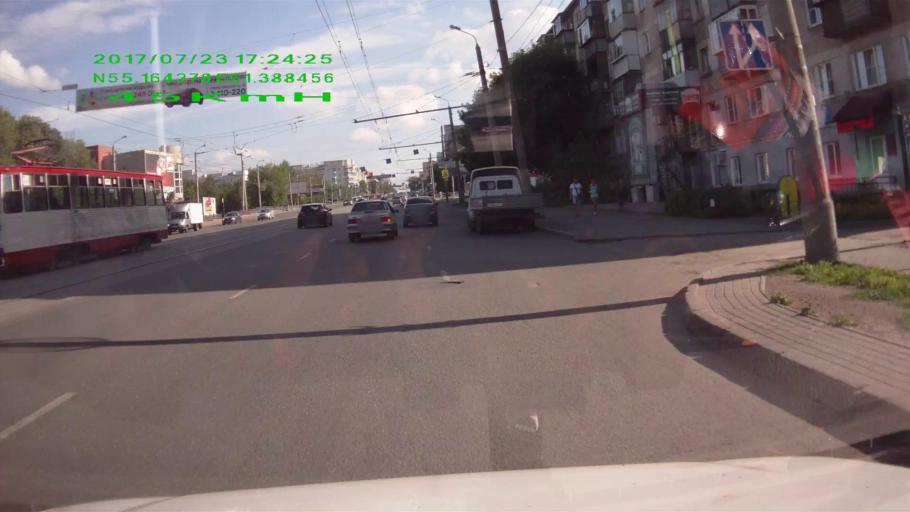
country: RU
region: Chelyabinsk
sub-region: Gorod Chelyabinsk
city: Chelyabinsk
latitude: 55.1640
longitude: 61.3884
